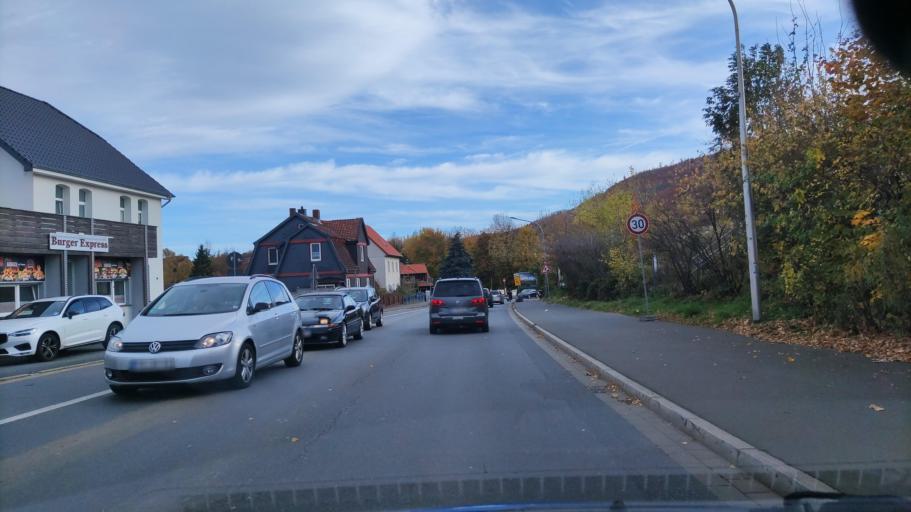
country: DE
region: Lower Saxony
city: Goslar
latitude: 51.9048
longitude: 10.4797
